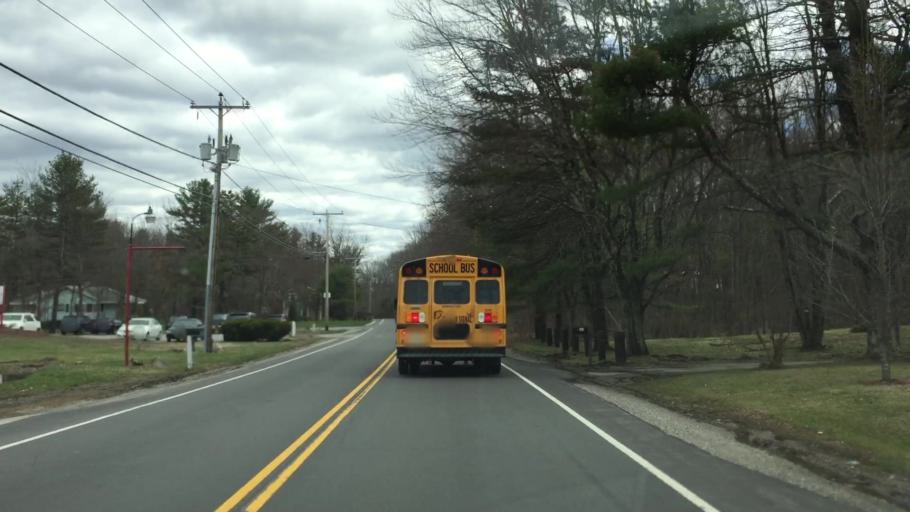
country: US
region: New Hampshire
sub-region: Rockingham County
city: Londonderry
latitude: 42.8149
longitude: -71.3596
